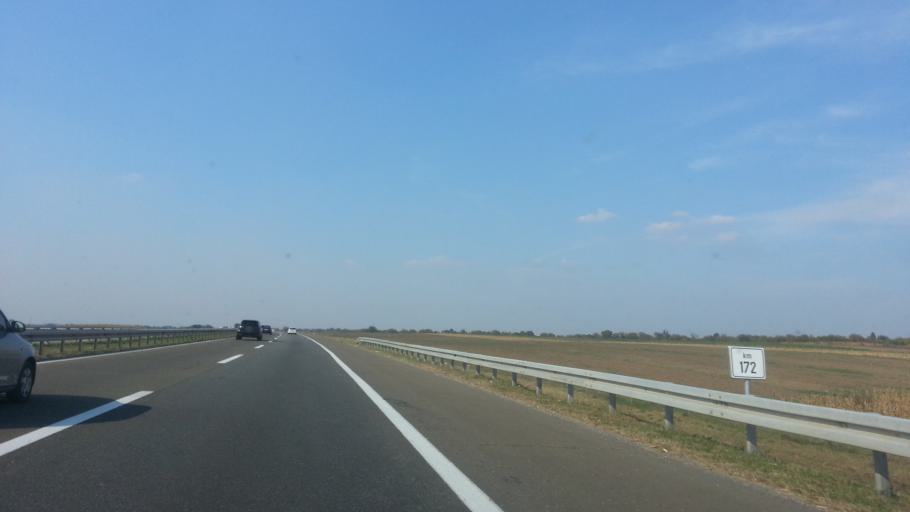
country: RS
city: Novi Banovci
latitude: 44.9254
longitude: 20.3023
